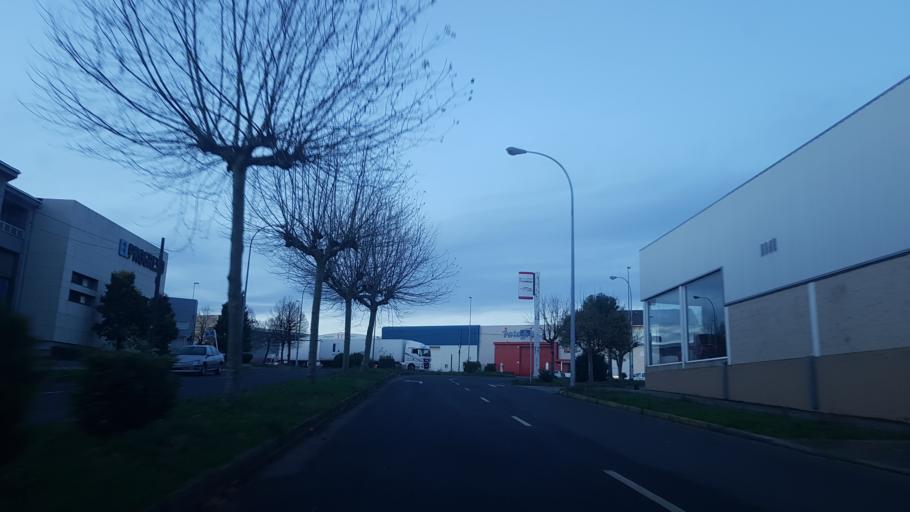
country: ES
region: Galicia
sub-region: Provincia de Lugo
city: Lugo
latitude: 43.0464
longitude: -7.5713
